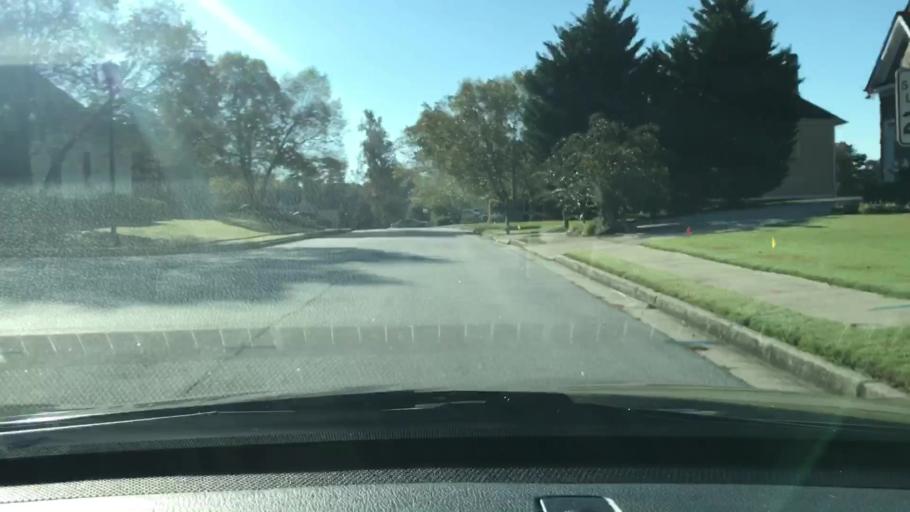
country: US
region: Georgia
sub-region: Douglas County
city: Douglasville
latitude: 33.7400
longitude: -84.7583
